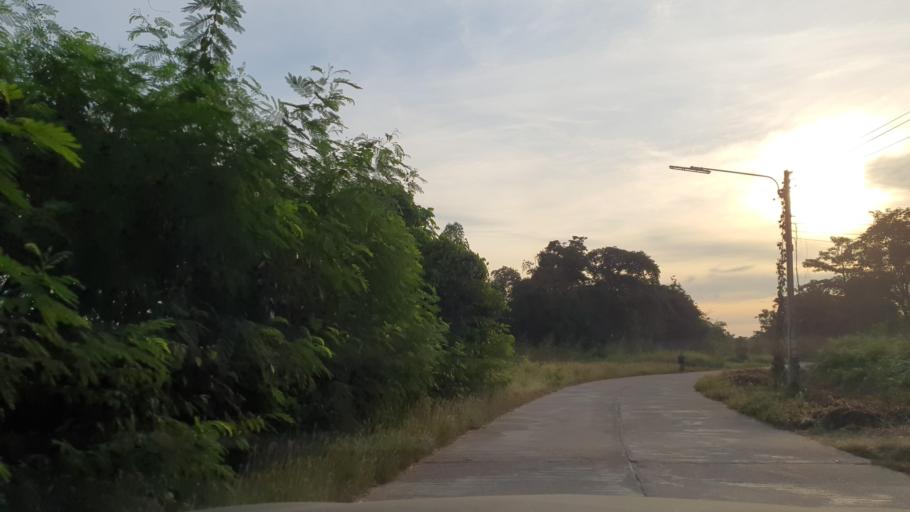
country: TH
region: Nakhon Sawan
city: Krok Phra
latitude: 15.6629
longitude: 100.0146
